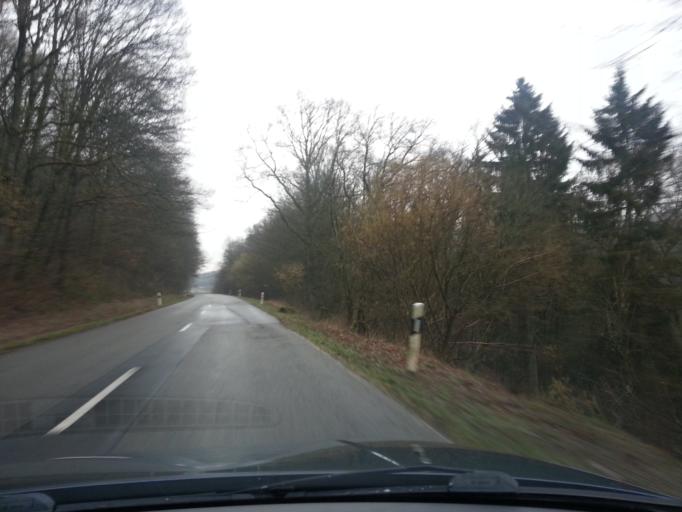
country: DE
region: Saarland
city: Freisen
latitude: 49.4956
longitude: 7.2317
